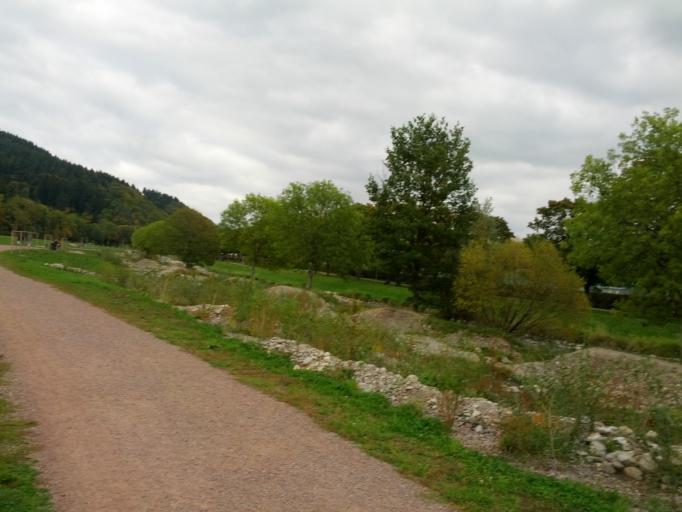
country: DE
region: Baden-Wuerttemberg
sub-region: Freiburg Region
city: Freiburg
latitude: 47.9919
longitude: 7.8849
